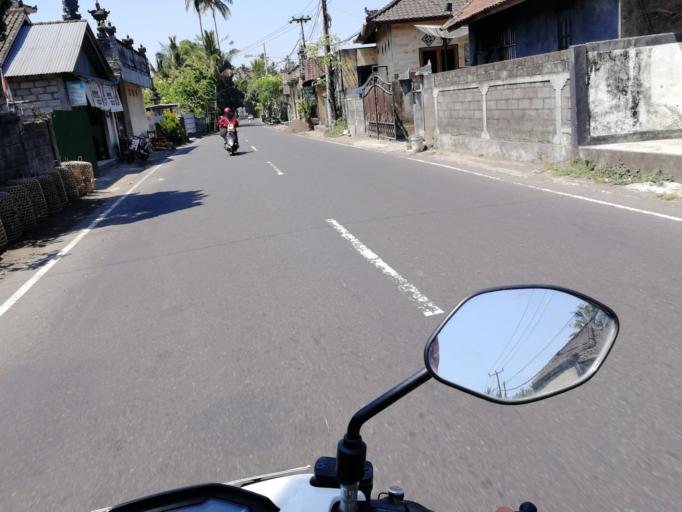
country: ID
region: Bali
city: Banjar Ababi
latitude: -8.3987
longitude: 115.5959
